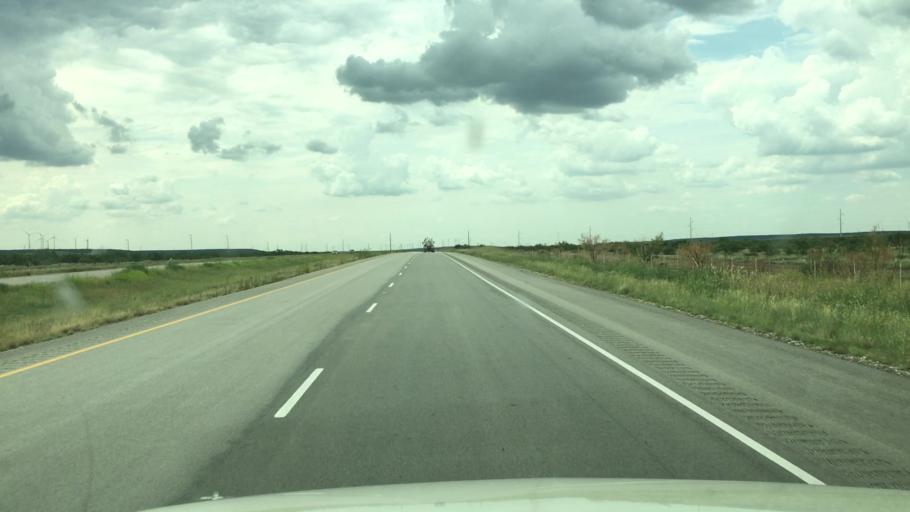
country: US
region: Texas
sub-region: Sterling County
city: Sterling City
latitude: 31.9561
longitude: -101.1975
